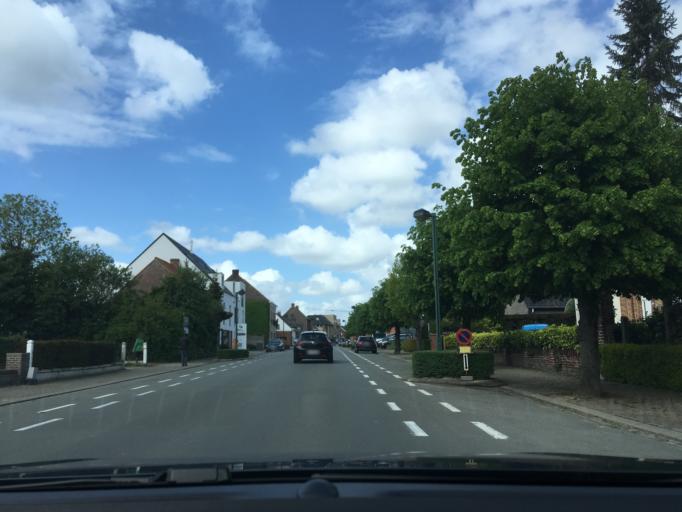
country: BE
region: Flanders
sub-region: Provincie West-Vlaanderen
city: Pittem
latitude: 50.9929
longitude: 3.2738
